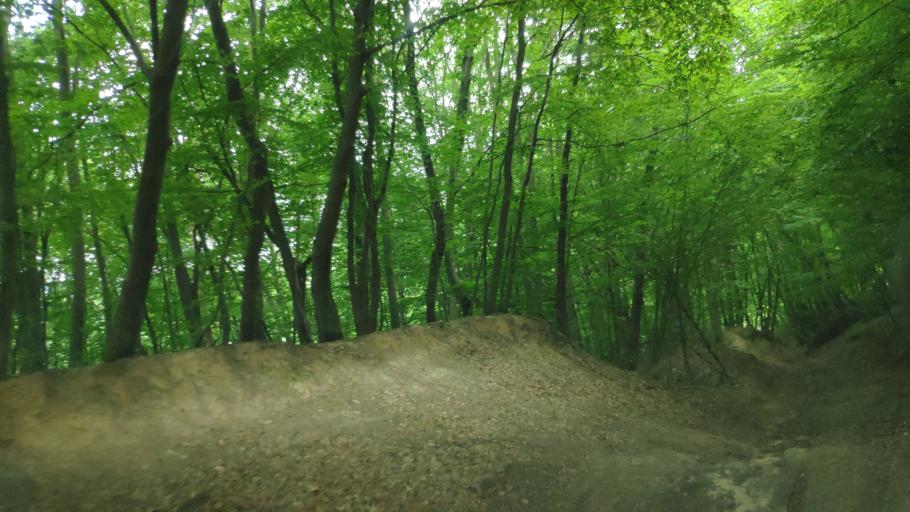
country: SK
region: Presovsky
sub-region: Okres Presov
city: Presov
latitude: 48.9588
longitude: 21.1385
